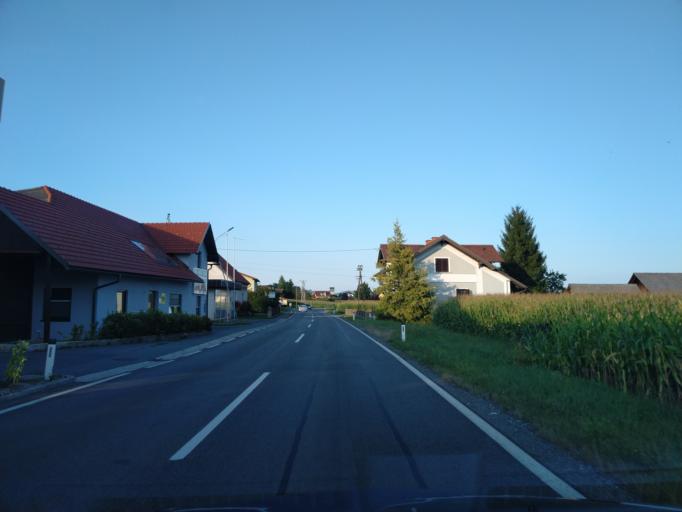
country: AT
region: Styria
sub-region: Politischer Bezirk Deutschlandsberg
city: Wies
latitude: 46.7263
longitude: 15.2867
